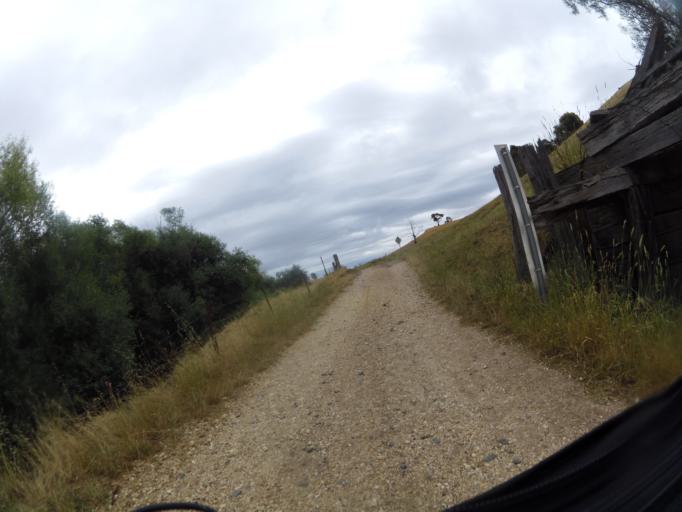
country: AU
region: Victoria
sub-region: Mount Alexander
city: Castlemaine
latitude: -37.2042
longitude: 144.0199
